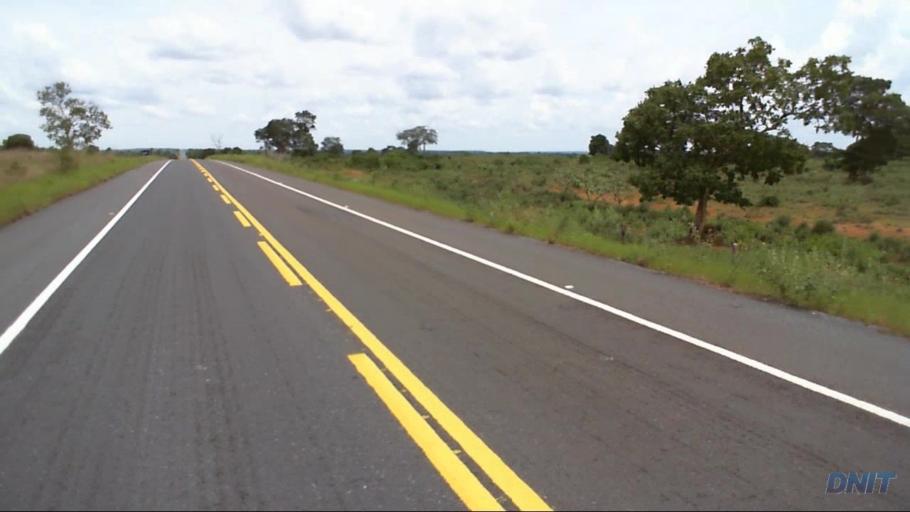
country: BR
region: Goias
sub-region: Sao Miguel Do Araguaia
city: Sao Miguel do Araguaia
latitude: -13.2903
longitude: -50.4252
